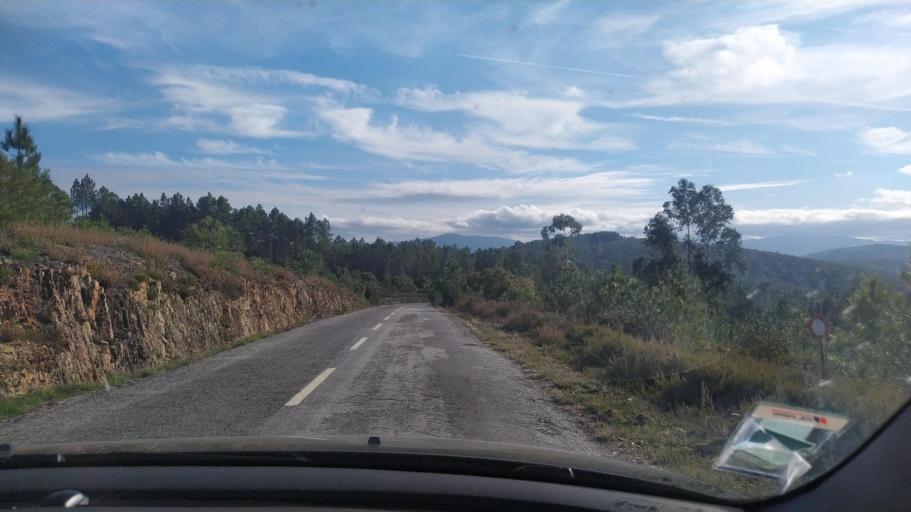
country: PT
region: Castelo Branco
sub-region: Concelho do Fundao
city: Aldeia de Joanes
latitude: 40.1939
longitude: -7.7228
